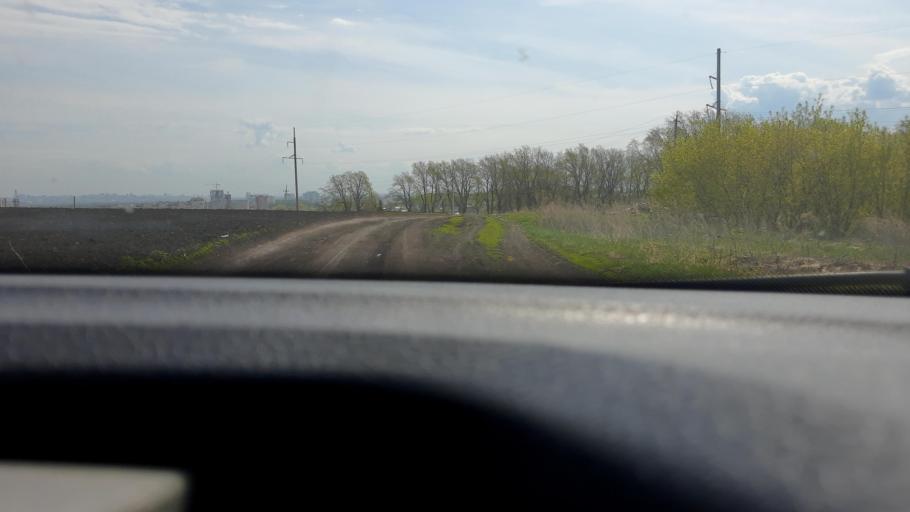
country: RU
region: Bashkortostan
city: Avdon
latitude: 54.7087
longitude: 55.7921
